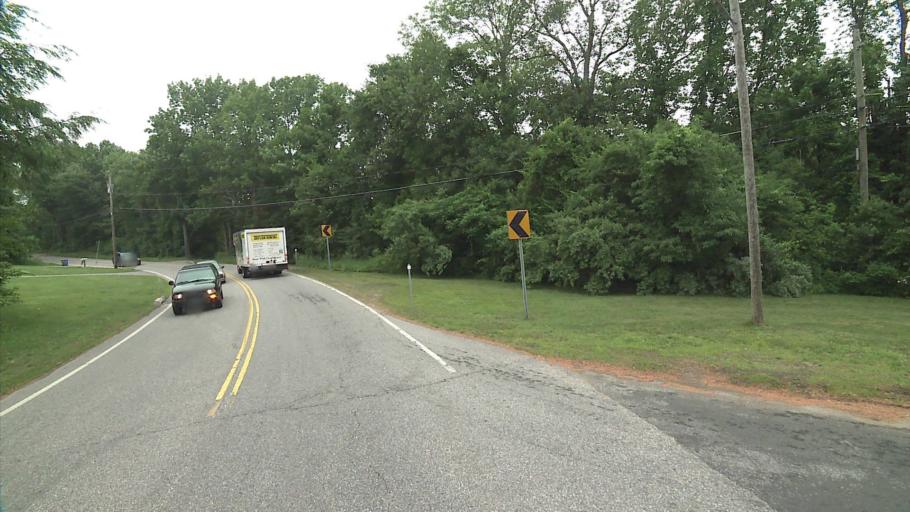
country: US
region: Connecticut
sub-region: Tolland County
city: Hebron
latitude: 41.6710
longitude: -72.3561
